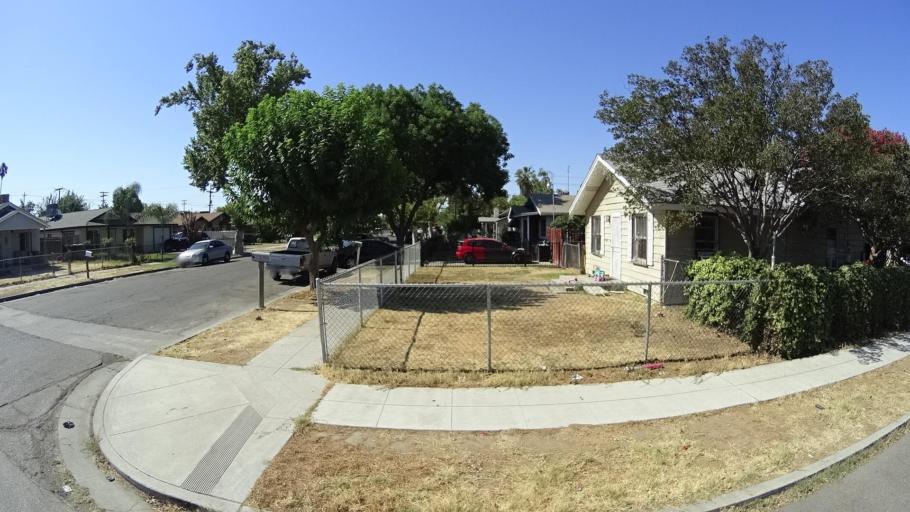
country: US
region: California
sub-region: Fresno County
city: Fresno
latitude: 36.7261
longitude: -119.7672
